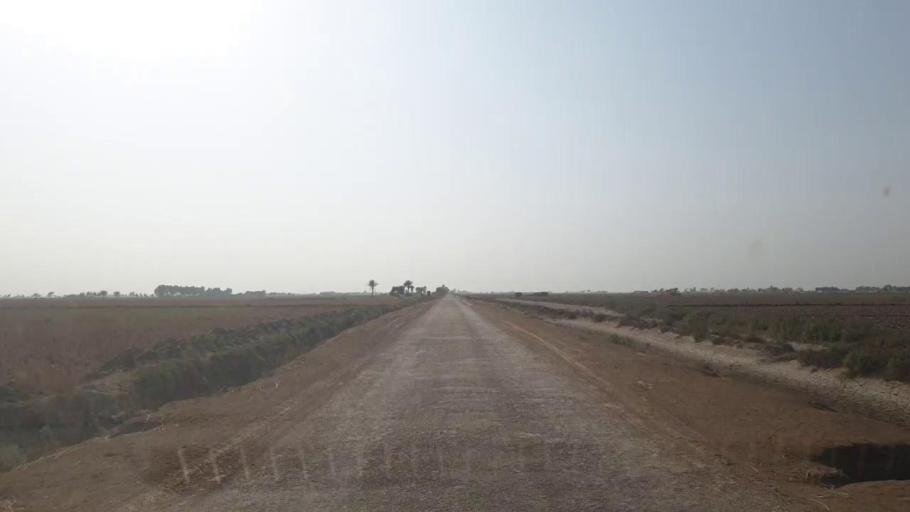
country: PK
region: Sindh
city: Kario
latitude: 24.5766
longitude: 68.5275
